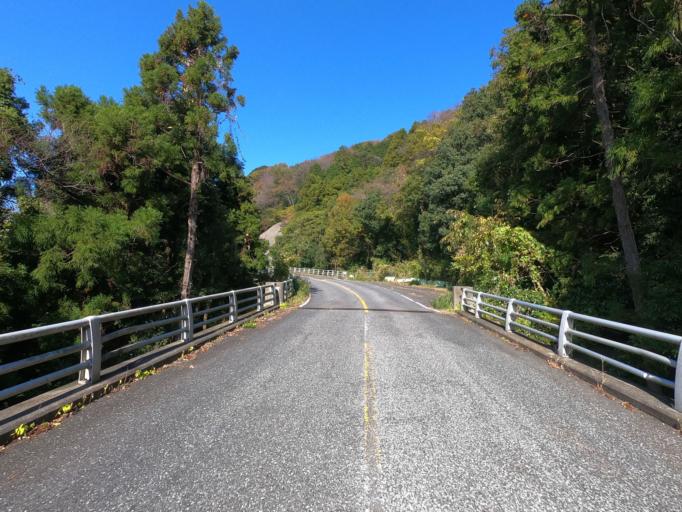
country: JP
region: Ibaraki
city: Tsukuba
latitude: 36.1693
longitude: 140.1746
